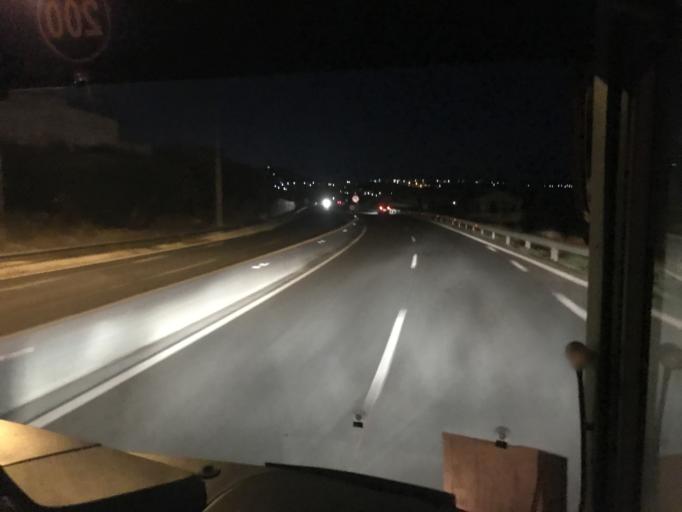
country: GR
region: Crete
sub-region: Nomos Irakleiou
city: Skalanion
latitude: 35.2666
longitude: 25.1848
